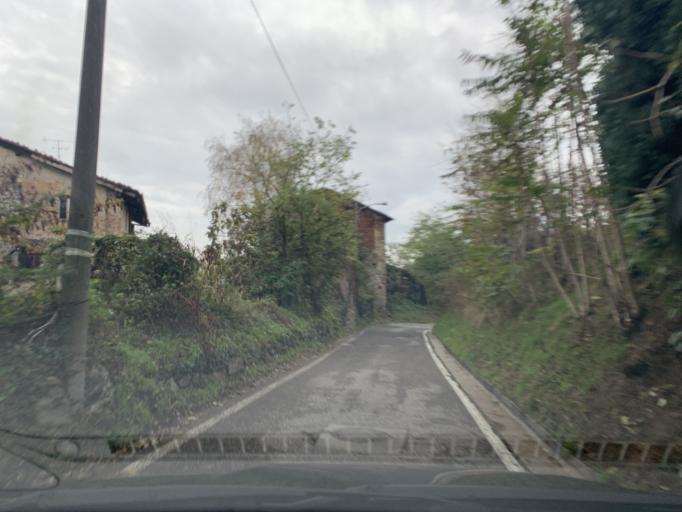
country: IT
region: Lombardy
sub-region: Provincia di Como
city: Casnate Con Bernate
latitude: 45.7474
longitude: 9.0704
